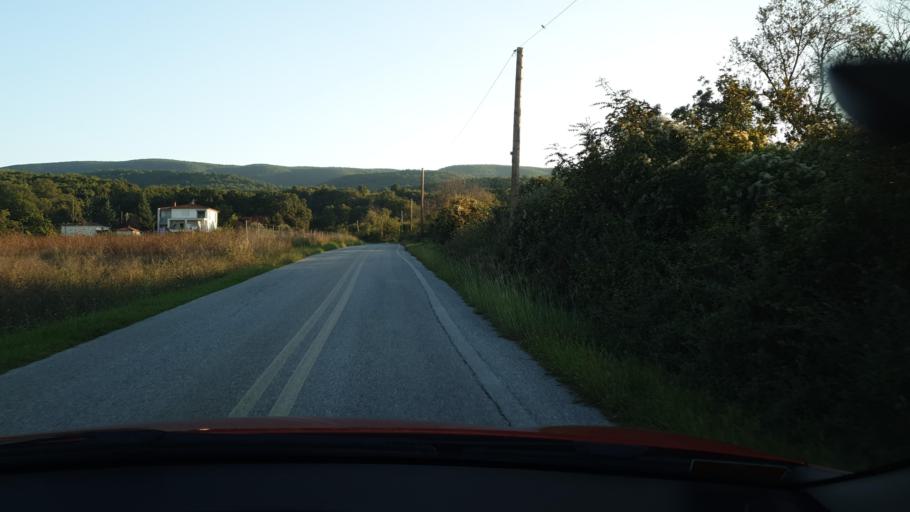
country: GR
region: Central Macedonia
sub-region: Nomos Thessalonikis
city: Gerakarou
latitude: 40.5622
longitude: 23.2820
